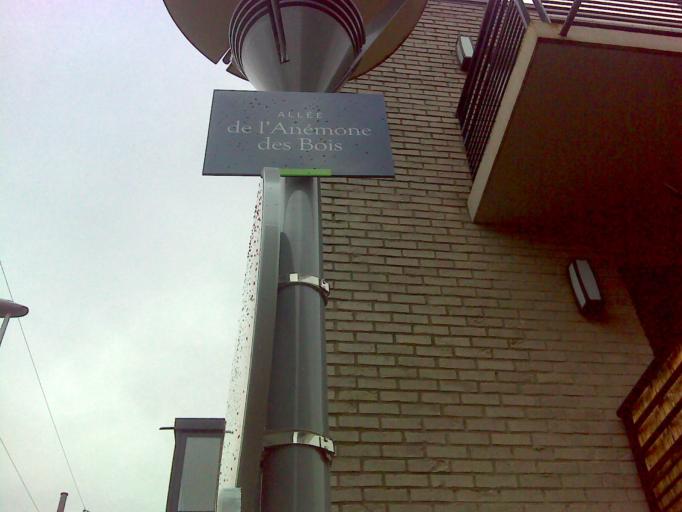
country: FR
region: Nord-Pas-de-Calais
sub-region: Departement du Nord
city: Wattignies
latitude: 50.5889
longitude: 3.0495
